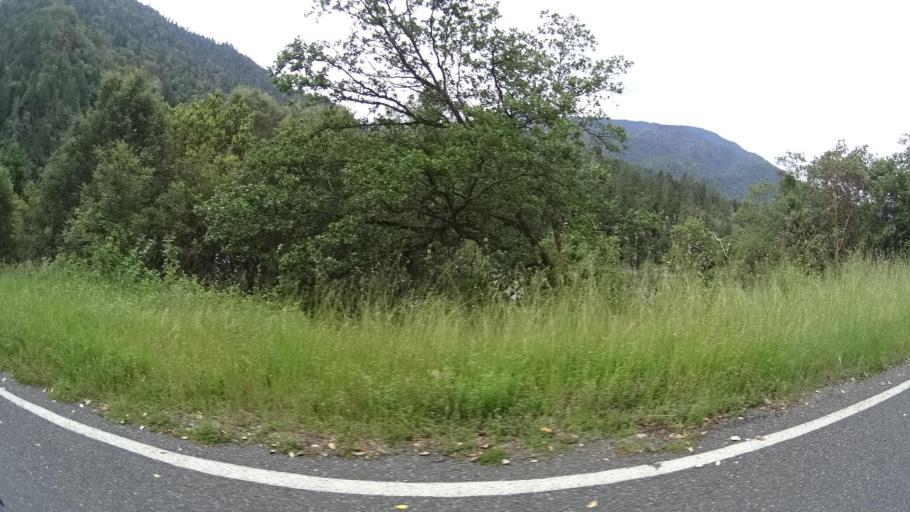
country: US
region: California
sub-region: Humboldt County
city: Willow Creek
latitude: 40.9491
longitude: -123.6124
